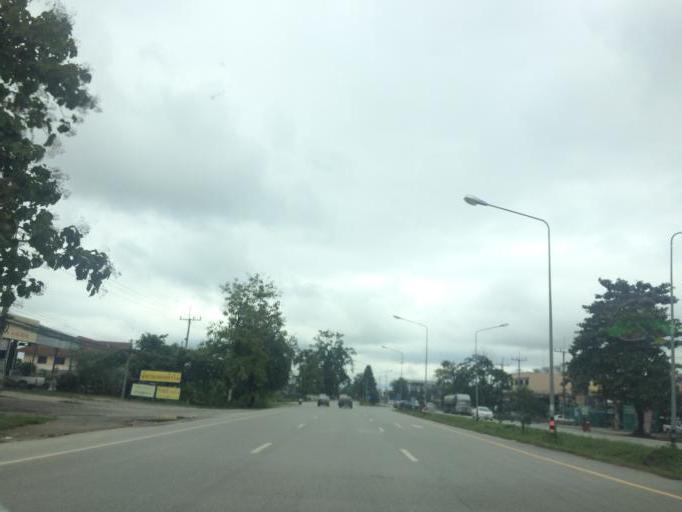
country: TH
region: Chiang Rai
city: Chiang Rai
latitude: 19.8579
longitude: 99.8171
